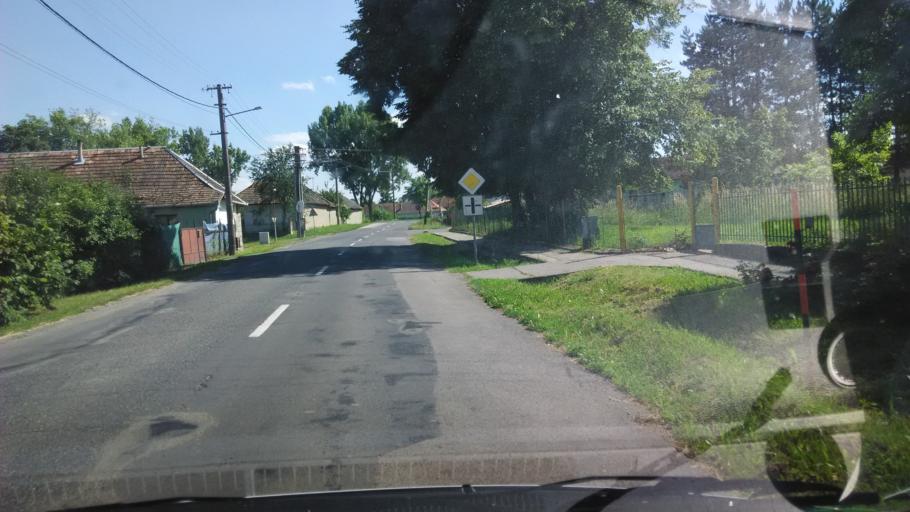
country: SK
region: Nitriansky
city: Tlmace
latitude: 48.1821
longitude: 18.4546
